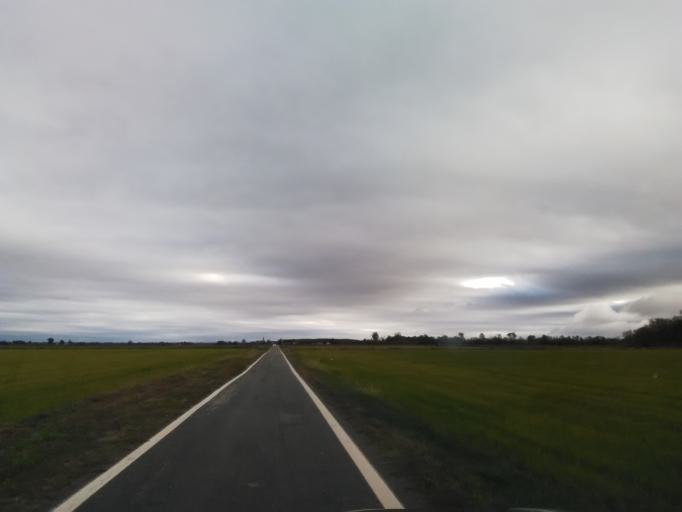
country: IT
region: Piedmont
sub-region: Provincia di Vercelli
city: Casanova Elvo
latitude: 45.4030
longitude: 8.2659
